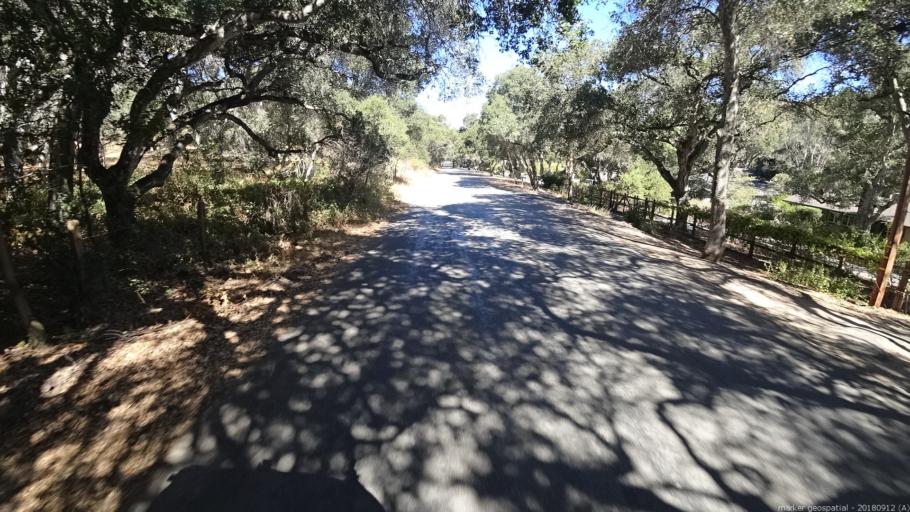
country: US
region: California
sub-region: Monterey County
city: Carmel Valley Village
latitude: 36.4852
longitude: -121.7470
